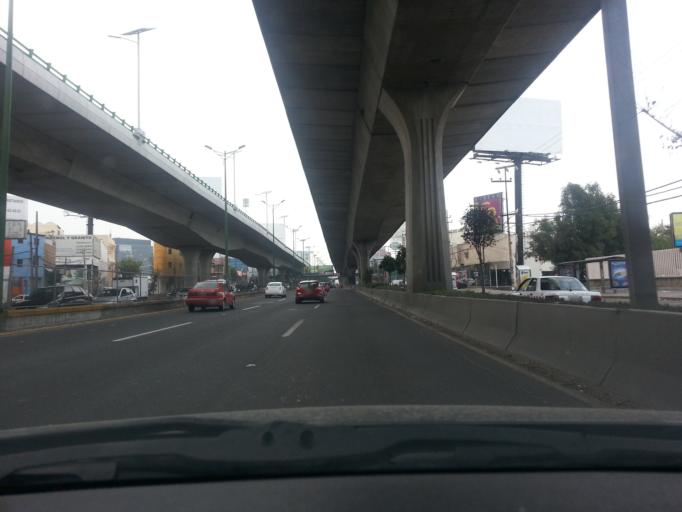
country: MX
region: Mexico
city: Naucalpan de Juarez
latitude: 19.4615
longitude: -99.2223
